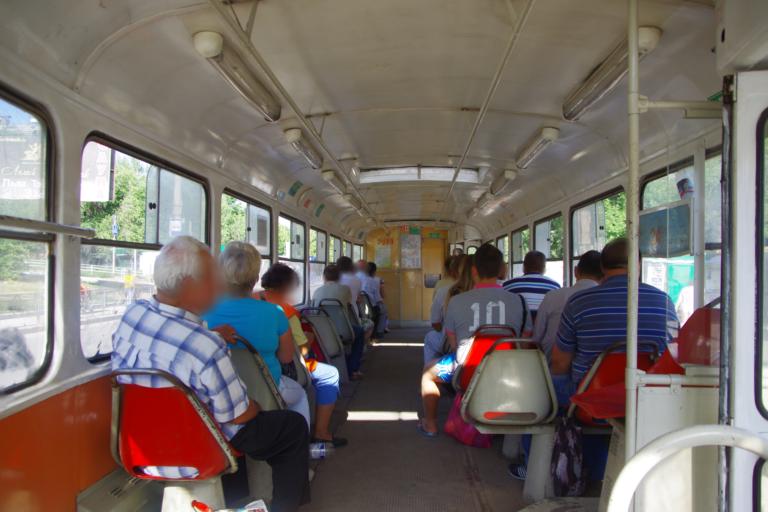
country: RU
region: Samara
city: Samara
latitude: 53.1921
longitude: 50.2059
